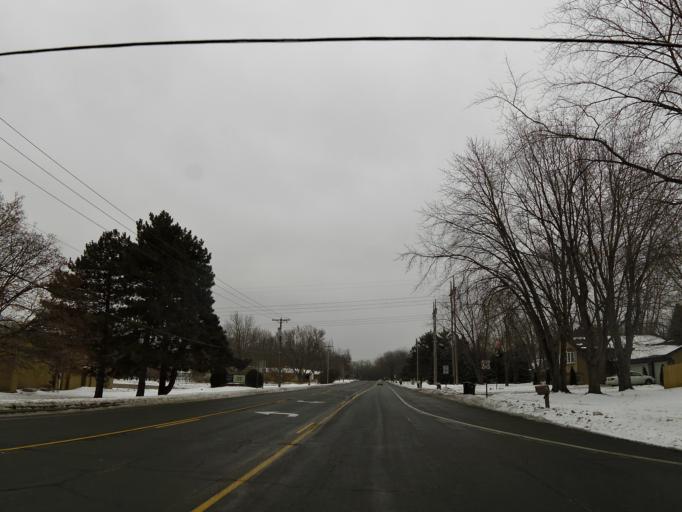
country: US
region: Minnesota
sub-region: Scott County
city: Savage
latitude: 44.7679
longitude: -93.3262
